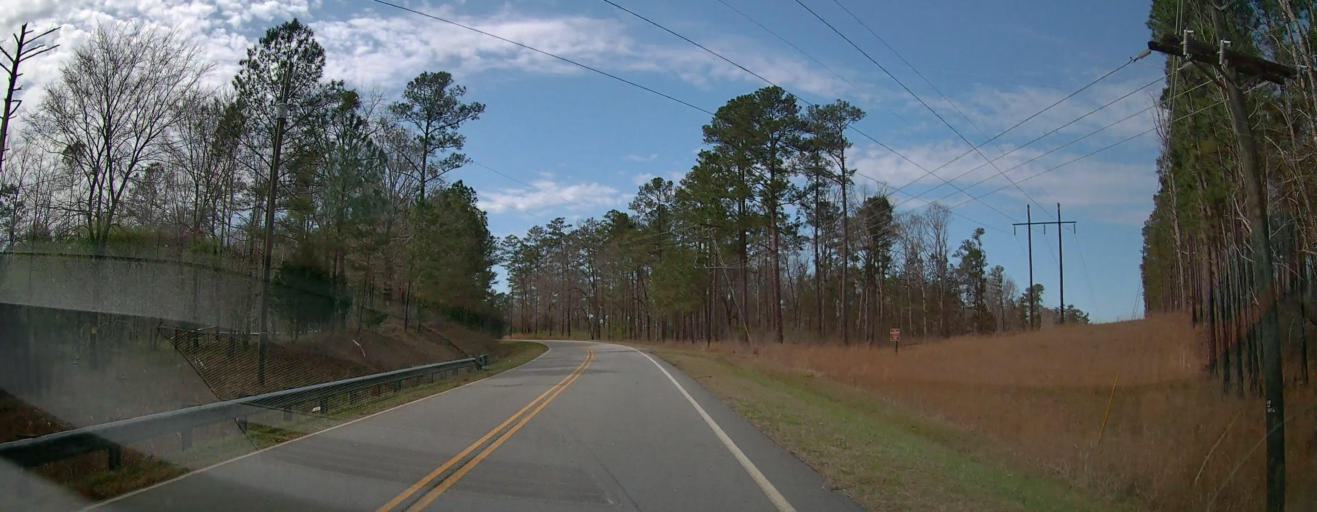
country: US
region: Georgia
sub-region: Monroe County
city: Forsyth
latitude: 33.0707
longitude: -83.7337
